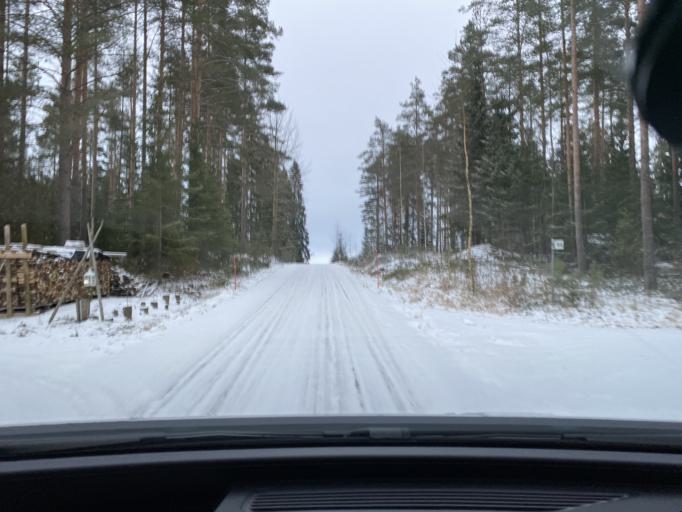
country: FI
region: Pirkanmaa
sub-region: Lounais-Pirkanmaa
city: Punkalaidun
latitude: 61.1213
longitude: 23.1163
